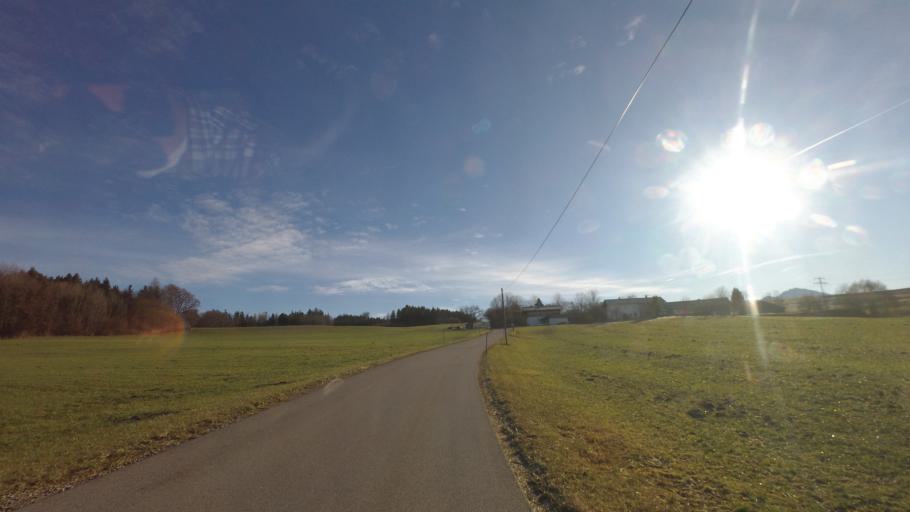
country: DE
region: Bavaria
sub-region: Upper Bavaria
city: Vachendorf
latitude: 47.8450
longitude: 12.5860
